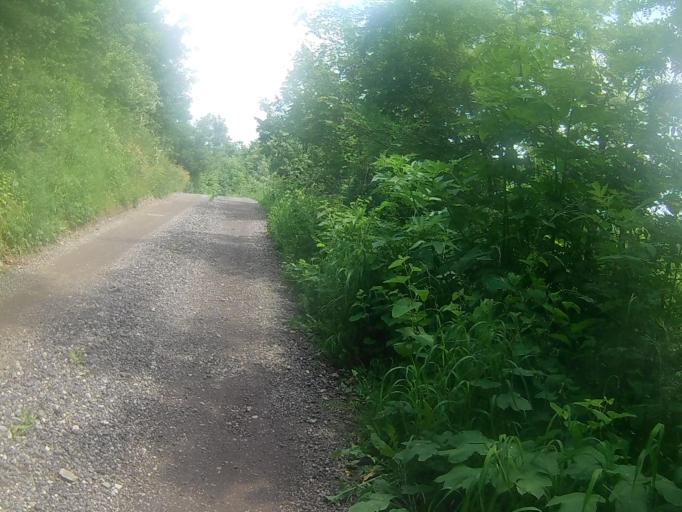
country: SI
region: Kungota
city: Zgornja Kungota
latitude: 46.6289
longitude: 15.5957
